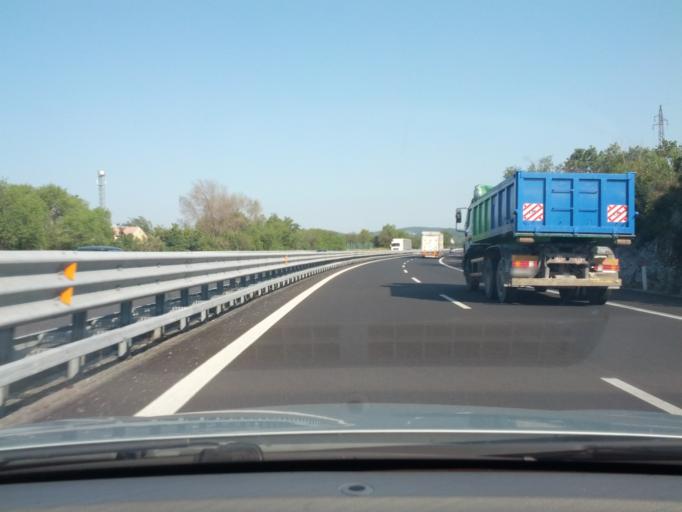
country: IT
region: Friuli Venezia Giulia
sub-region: Provincia di Trieste
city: Duino
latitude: 45.7794
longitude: 13.6003
